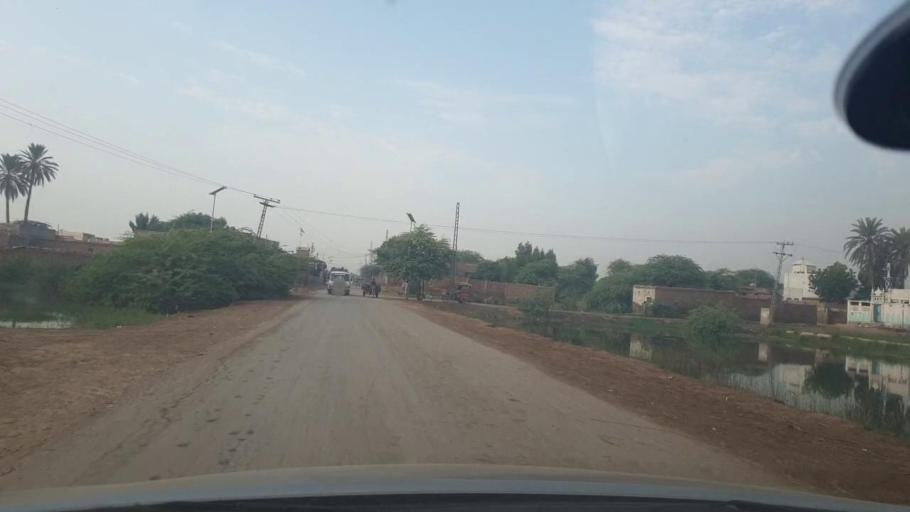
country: PK
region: Sindh
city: Jacobabad
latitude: 28.2688
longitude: 68.4199
